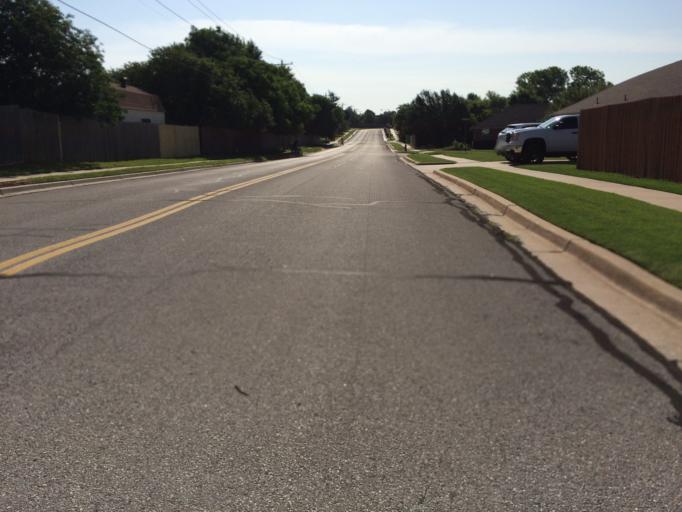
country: US
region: Oklahoma
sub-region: Cleveland County
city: Norman
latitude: 35.2400
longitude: -97.4924
